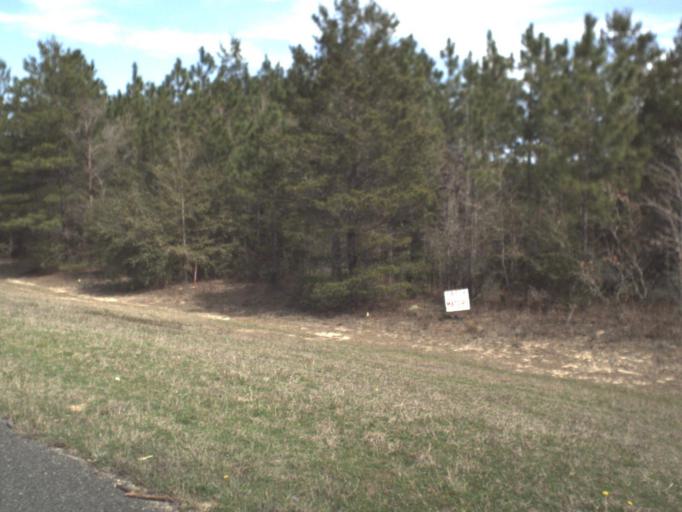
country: US
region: Florida
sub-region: Bay County
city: Youngstown
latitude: 30.5708
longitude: -85.3874
